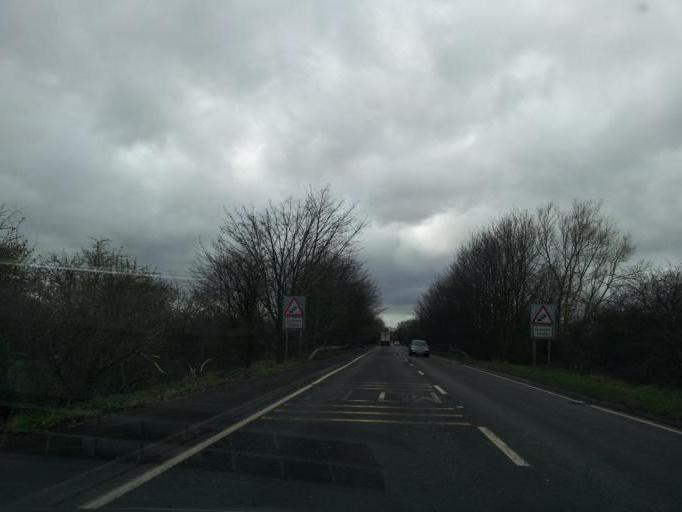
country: GB
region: England
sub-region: Somerset
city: Stoke-sub-Hamdon
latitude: 50.9622
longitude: -2.7280
